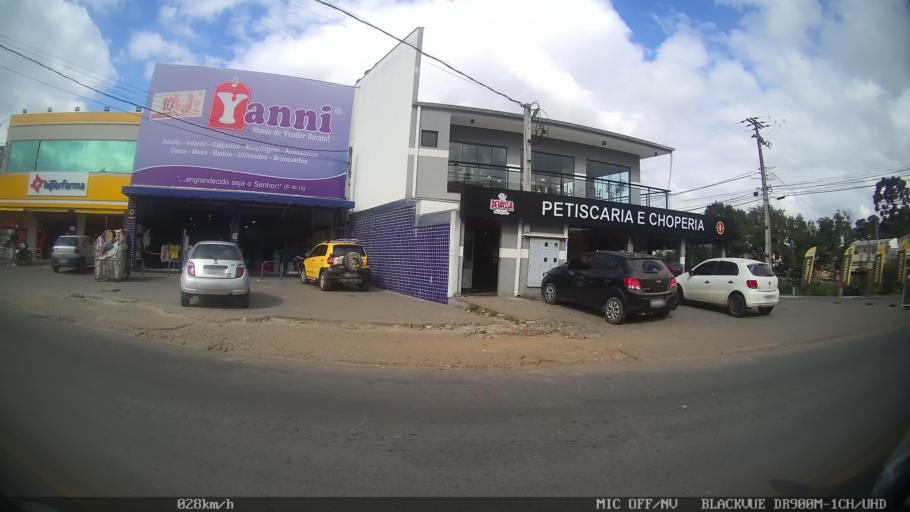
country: BR
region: Parana
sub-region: Colombo
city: Colombo
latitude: -25.3636
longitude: -49.2103
